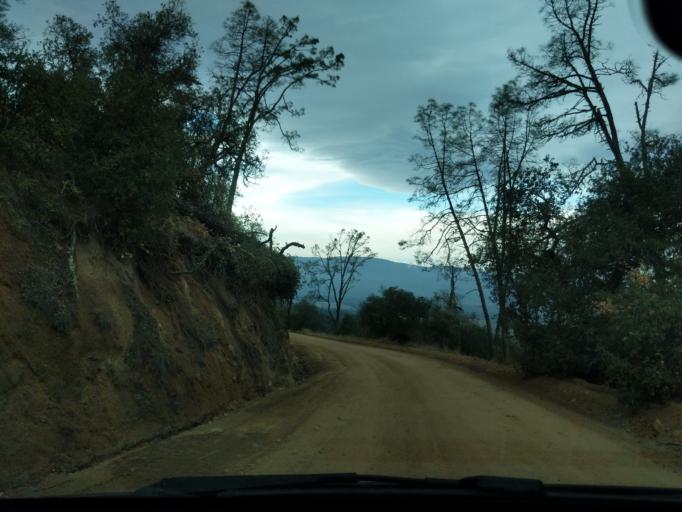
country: US
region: California
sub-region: Monterey County
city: Soledad
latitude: 36.5340
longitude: -121.3027
